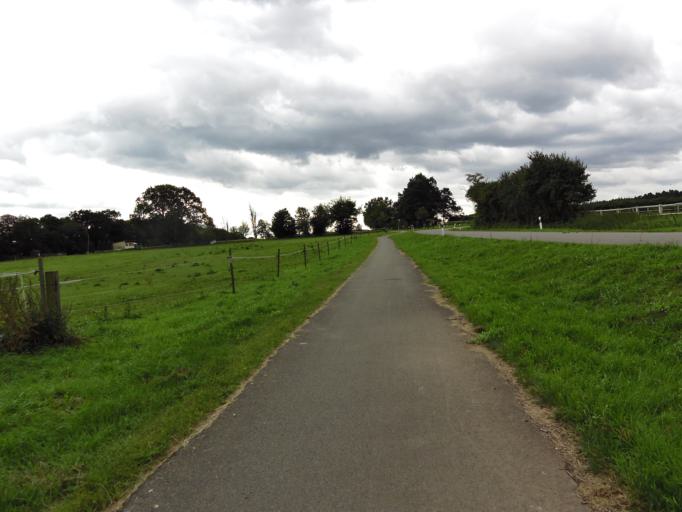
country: DE
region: Saxony-Anhalt
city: Arneburg
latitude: 52.6294
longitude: 12.0029
